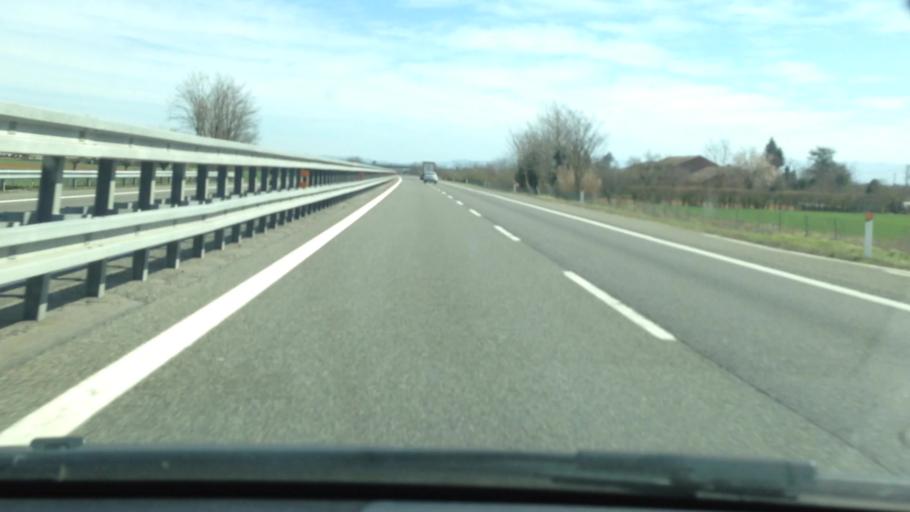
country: IT
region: Piedmont
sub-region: Provincia di Alessandria
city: San Giuliano Vecchio
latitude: 44.9181
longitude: 8.7449
